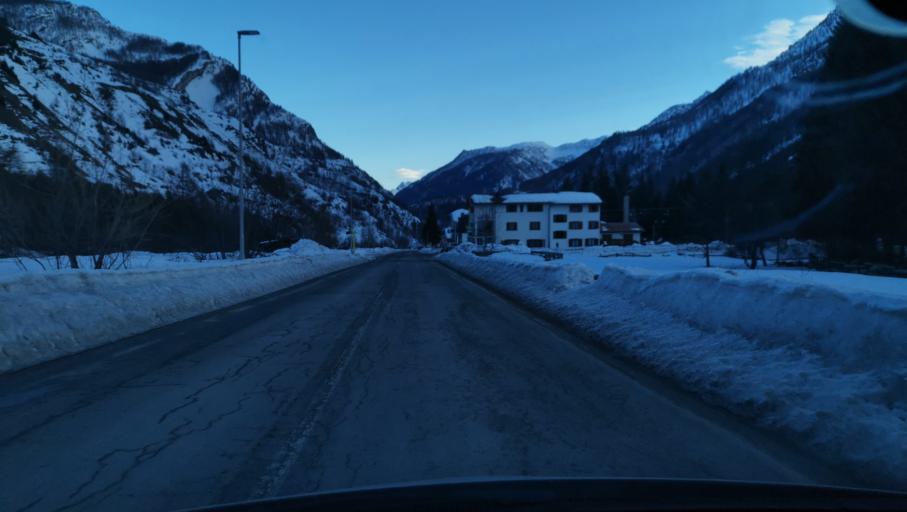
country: IT
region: Piedmont
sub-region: Provincia di Cuneo
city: Bersezio
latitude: 44.3695
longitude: 6.9824
